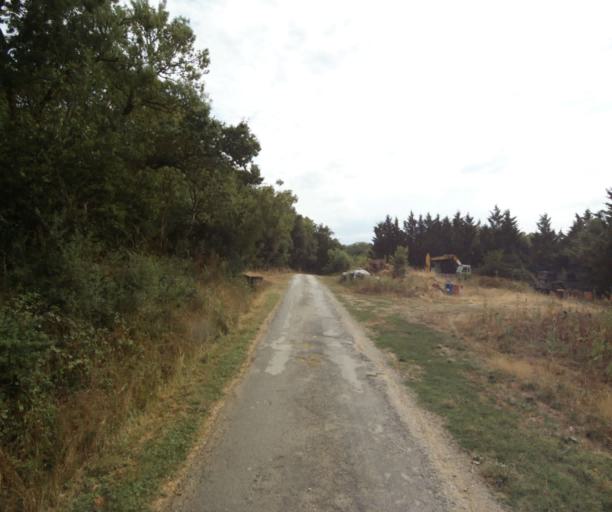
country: FR
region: Midi-Pyrenees
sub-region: Departement de la Haute-Garonne
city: Revel
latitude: 43.4261
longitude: 1.9773
